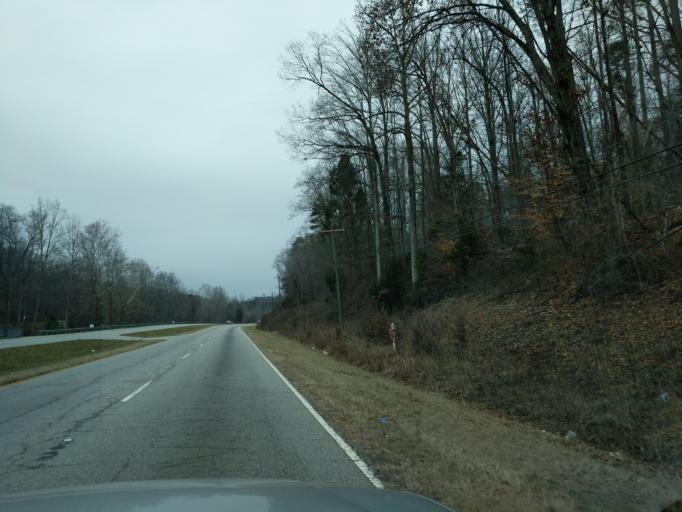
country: US
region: South Carolina
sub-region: Greenville County
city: Tigerville
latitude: 35.0639
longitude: -82.4309
